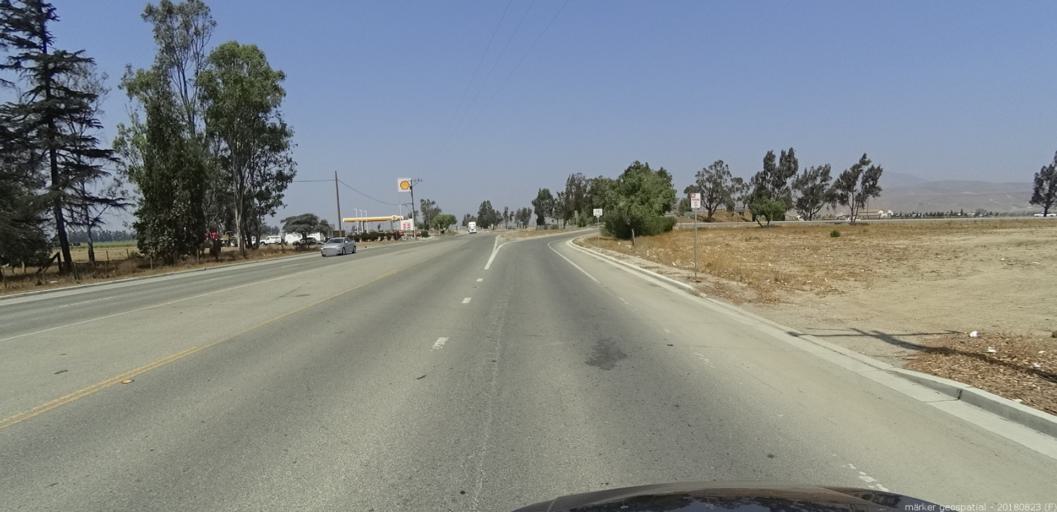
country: US
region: California
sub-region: Monterey County
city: Greenfield
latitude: 36.3373
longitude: -121.2556
